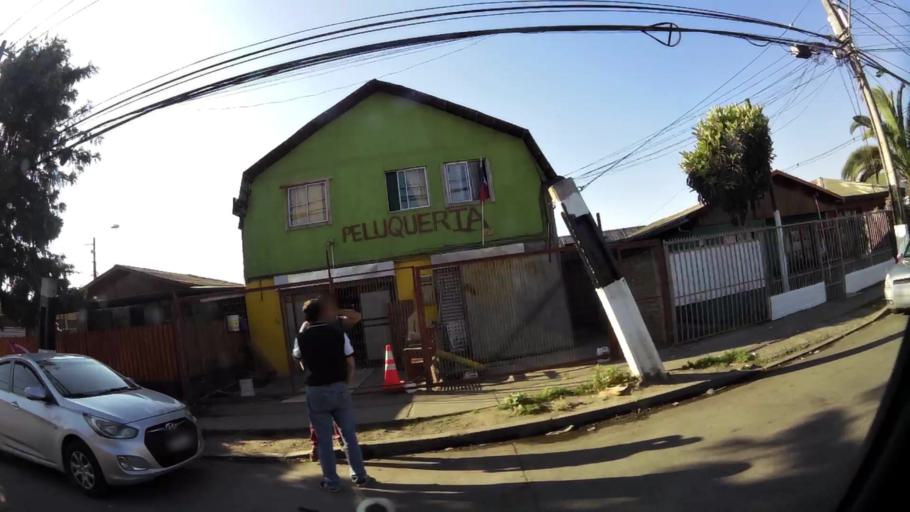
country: CL
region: Santiago Metropolitan
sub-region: Provincia de Santiago
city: Lo Prado
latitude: -33.4880
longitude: -70.7629
